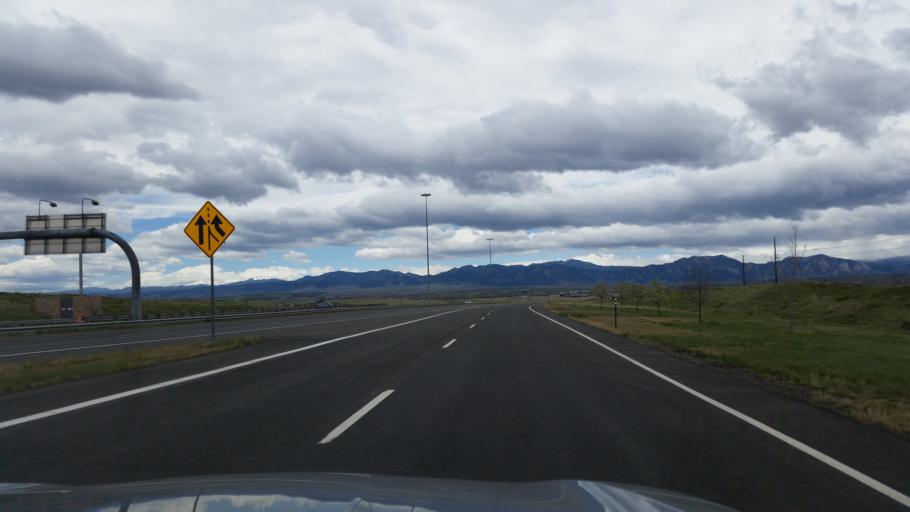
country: US
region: Colorado
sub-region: Boulder County
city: Lafayette
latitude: 39.9801
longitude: -105.0425
